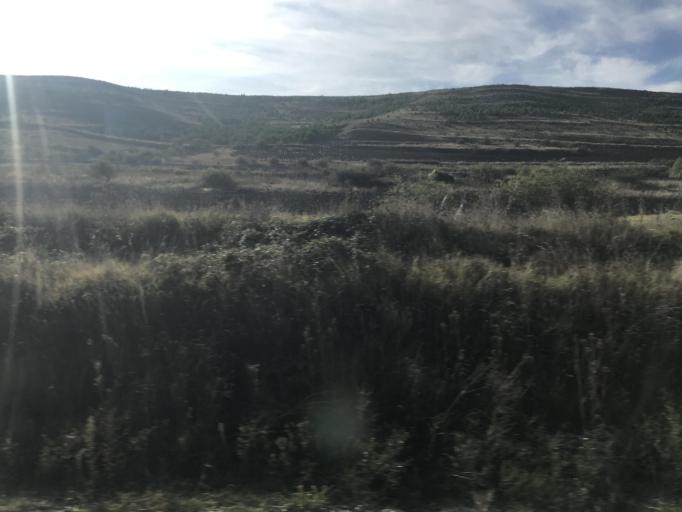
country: ES
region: Castille and Leon
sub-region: Provincia de Burgos
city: Villanueva de Teba
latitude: 42.6251
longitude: -3.1583
